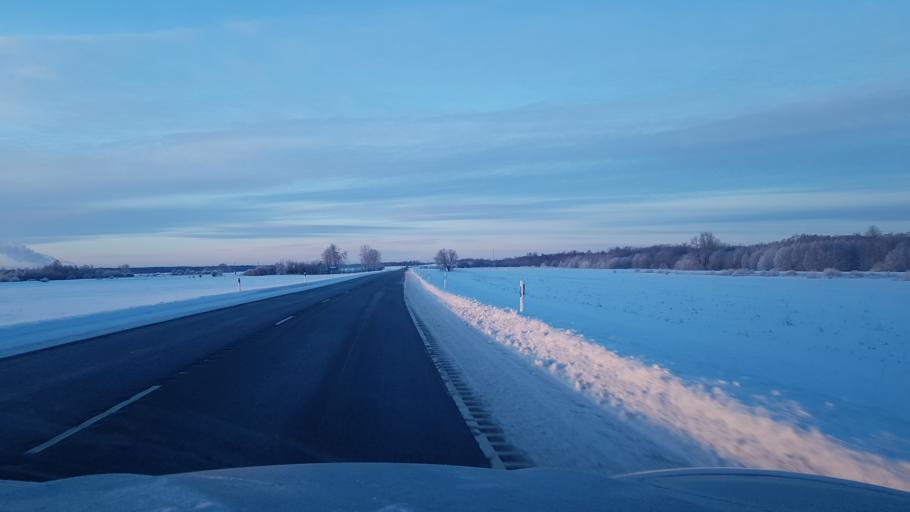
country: EE
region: Ida-Virumaa
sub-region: Narva-Joesuu linn
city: Narva-Joesuu
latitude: 59.4013
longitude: 28.0137
